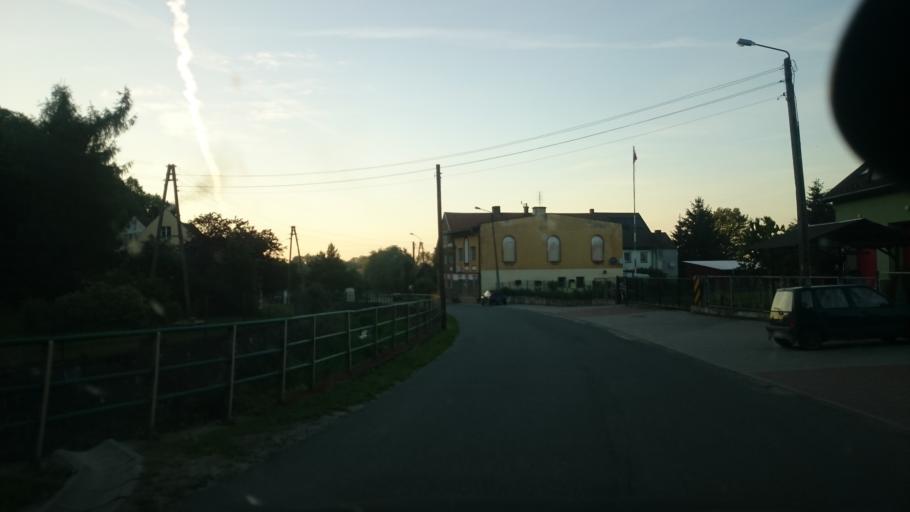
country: PL
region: Lower Silesian Voivodeship
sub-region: Powiat zabkowicki
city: Zloty Stok
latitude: 50.4589
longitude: 16.8488
